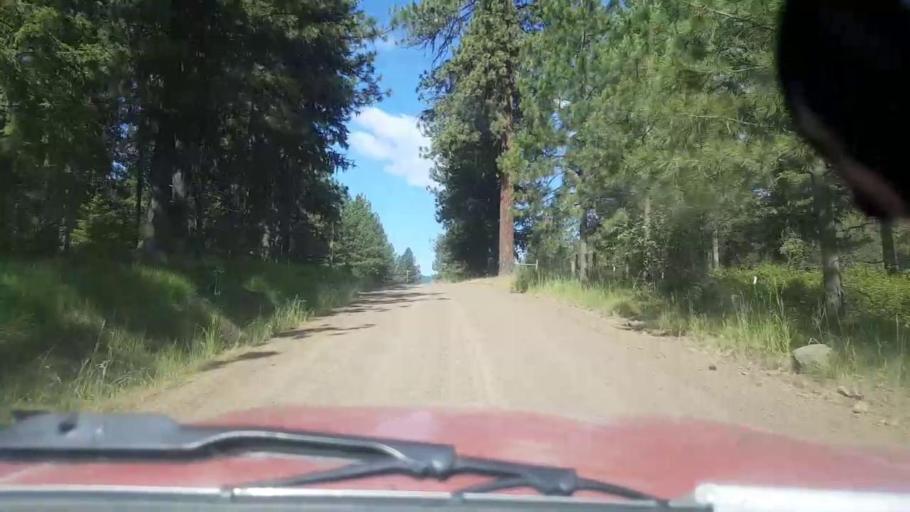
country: US
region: Washington
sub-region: Garfield County
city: Pomeroy
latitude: 46.0371
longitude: -117.4173
